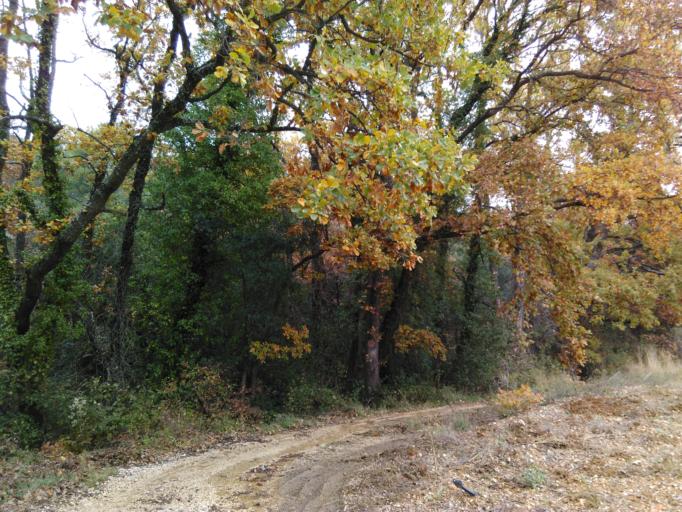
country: FR
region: Provence-Alpes-Cote d'Azur
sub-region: Departement du Vaucluse
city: Venasque
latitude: 43.9946
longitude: 5.1671
